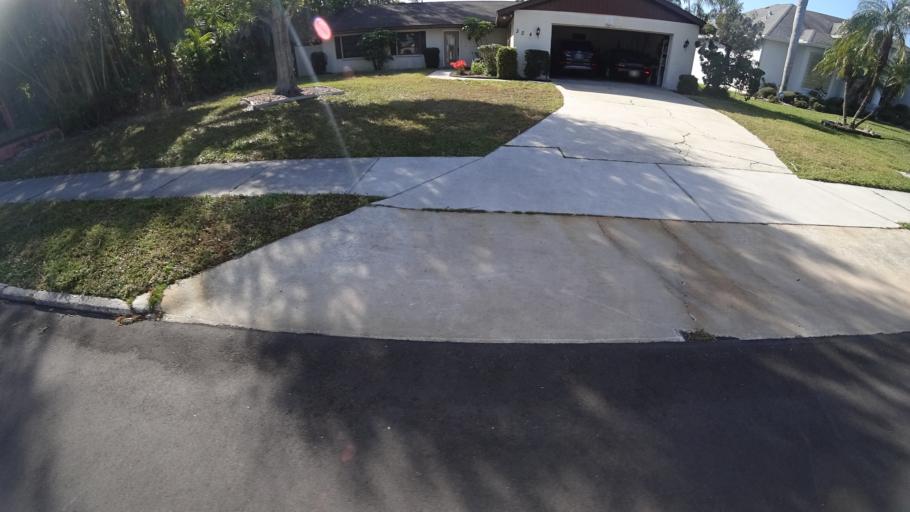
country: US
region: Florida
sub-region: Manatee County
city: Whitfield
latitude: 27.4135
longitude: -82.5701
